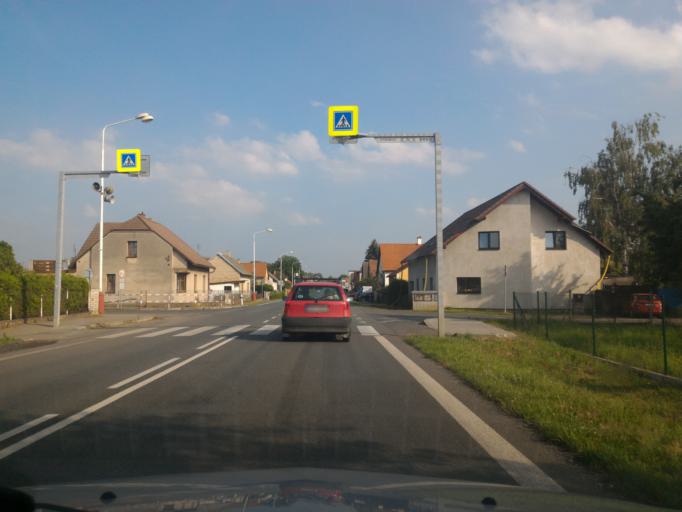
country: CZ
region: Central Bohemia
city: Zleby
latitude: 49.8708
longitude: 15.4357
